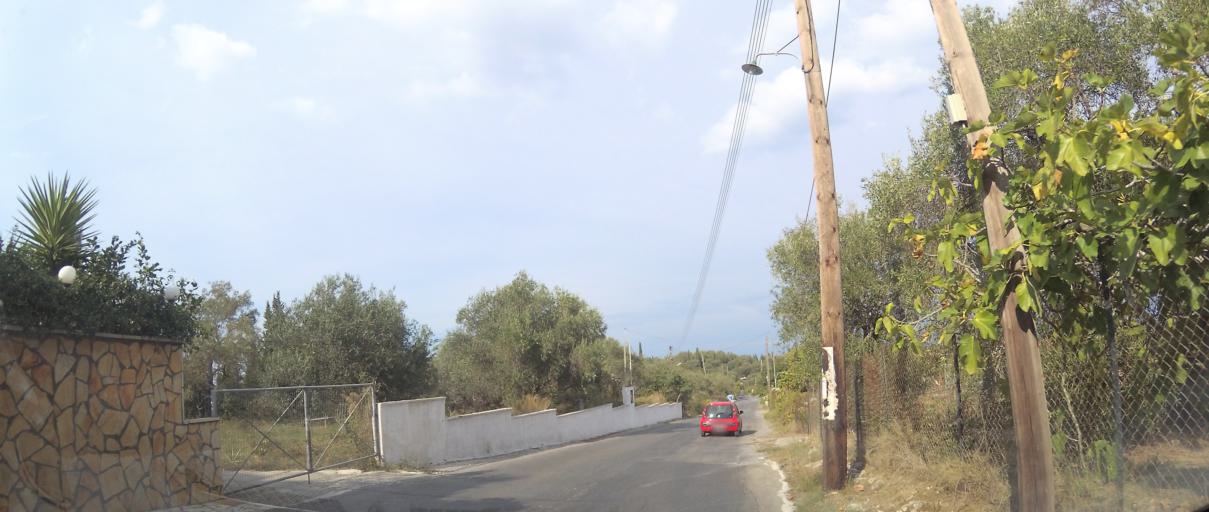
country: GR
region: Ionian Islands
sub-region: Nomos Kerkyras
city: Kynopiastes
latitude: 39.5601
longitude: 19.8621
